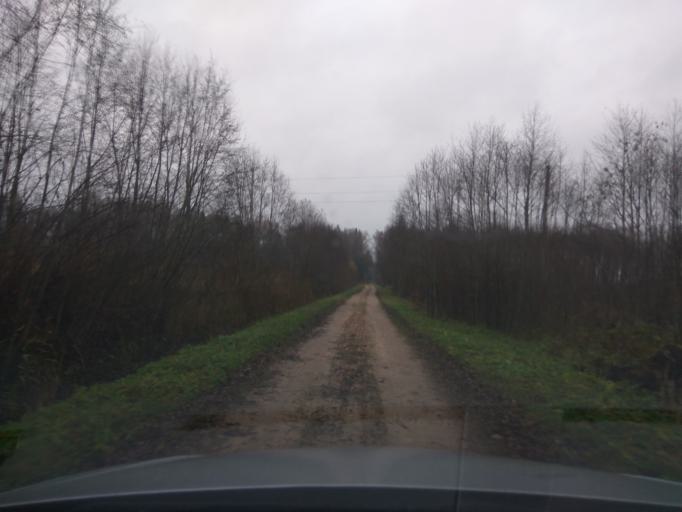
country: LV
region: Kuldigas Rajons
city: Kuldiga
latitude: 56.9240
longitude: 21.9737
